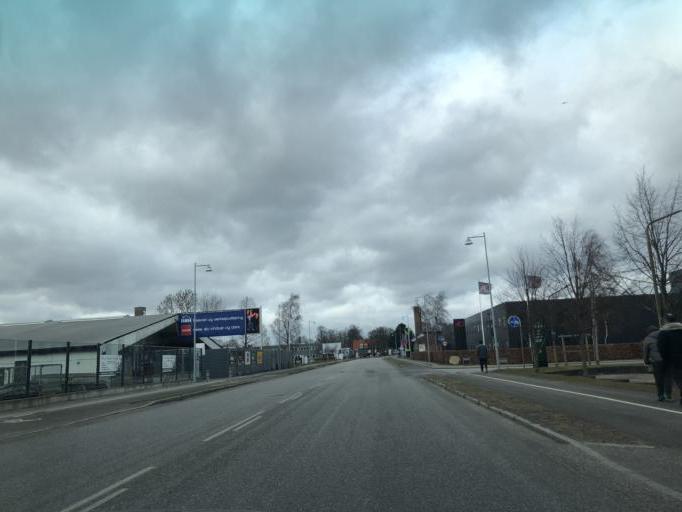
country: DK
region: Capital Region
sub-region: Albertslund Kommune
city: Albertslund
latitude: 55.6647
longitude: 12.3610
